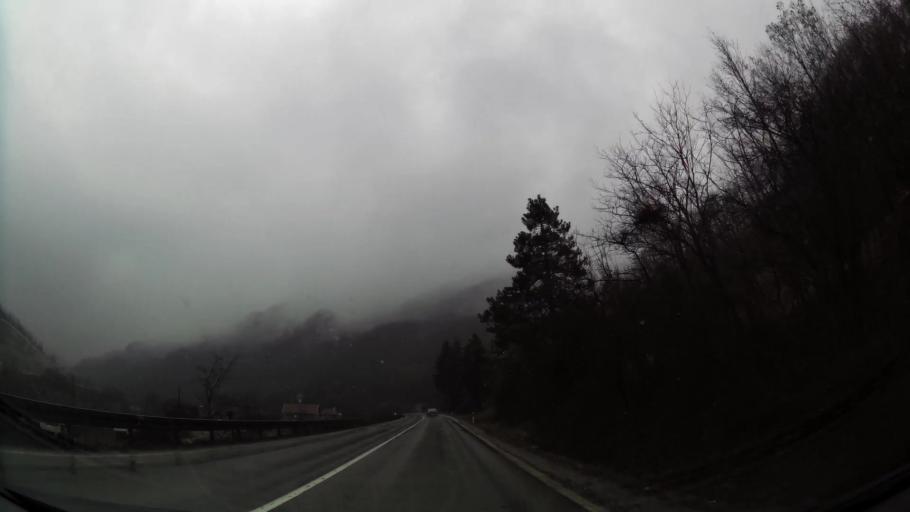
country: RS
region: Central Serbia
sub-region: Jablanicki Okrug
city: Vlasotince
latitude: 42.8724
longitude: 22.1037
